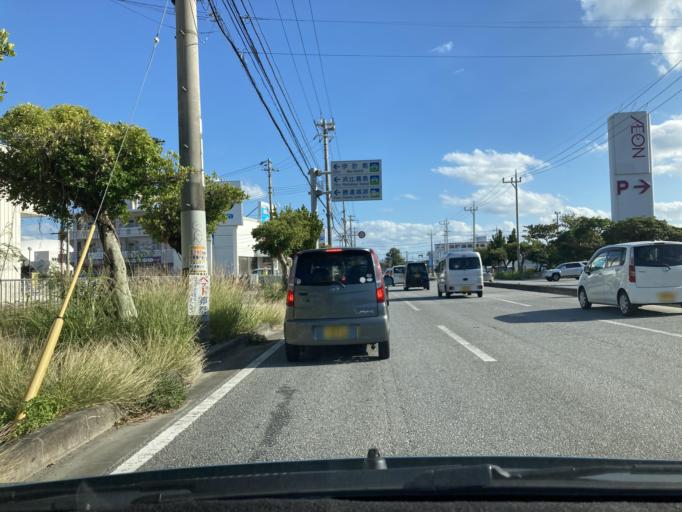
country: JP
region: Okinawa
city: Katsuren-haebaru
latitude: 26.3393
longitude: 127.8458
